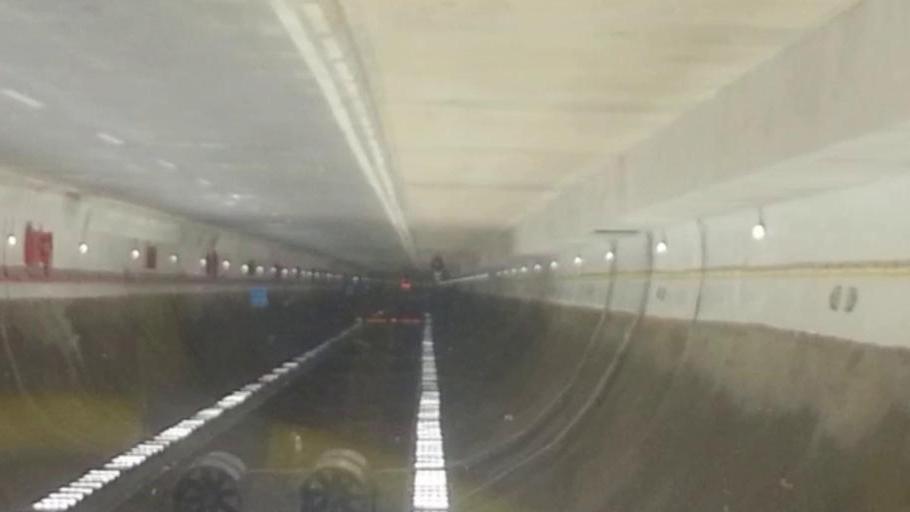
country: BR
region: Rio de Janeiro
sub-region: Nilopolis
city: Nilopolis
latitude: -22.9108
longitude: -43.4007
